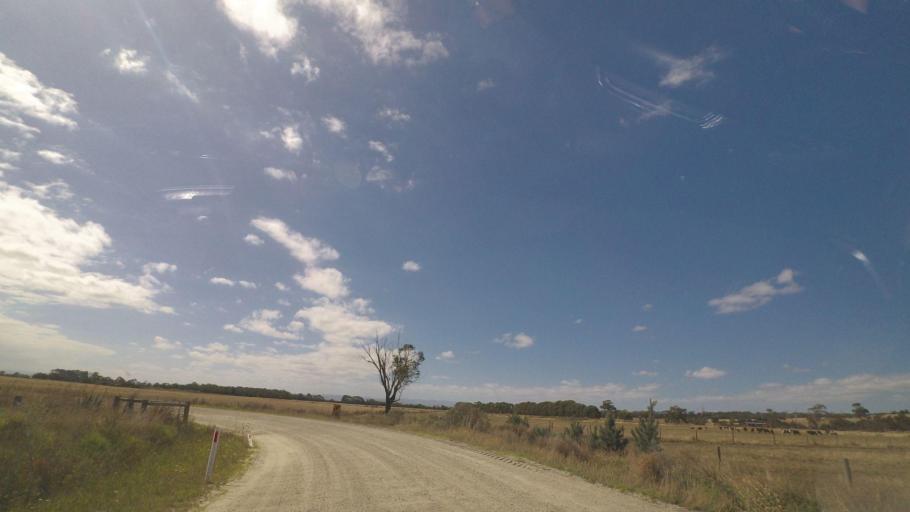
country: AU
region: Victoria
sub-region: Cardinia
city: Bunyip
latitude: -38.2631
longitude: 145.6676
